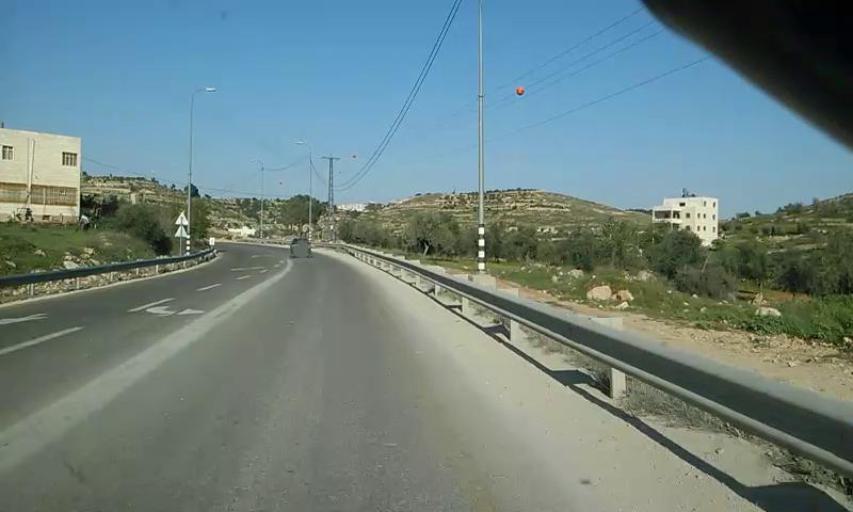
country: PS
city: Khallat ad Dar
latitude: 31.5019
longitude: 35.1215
